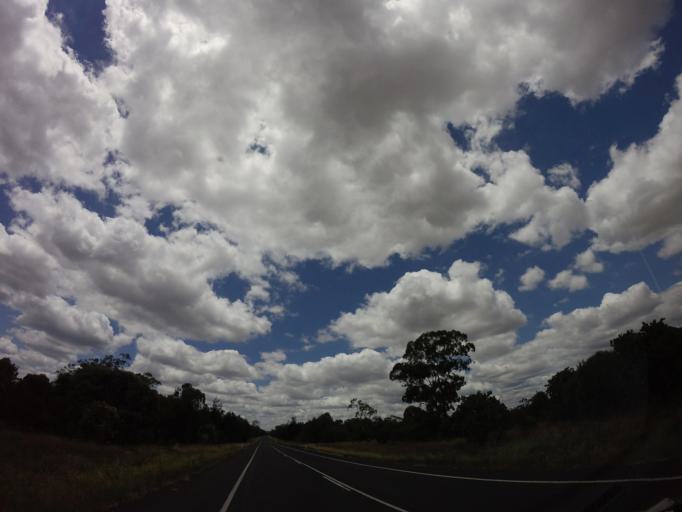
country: AU
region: Queensland
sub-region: Goondiwindi
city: Goondiwindi
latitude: -28.0532
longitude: 150.7770
